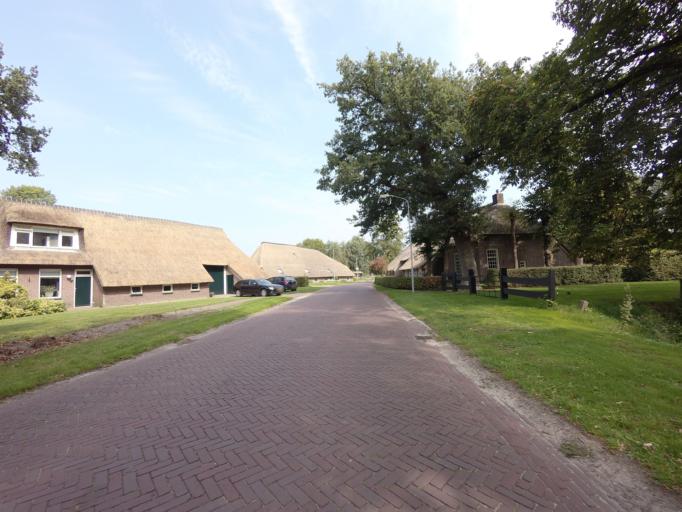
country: NL
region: Drenthe
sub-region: Gemeente Assen
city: Assen
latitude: 52.9739
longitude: 6.6268
